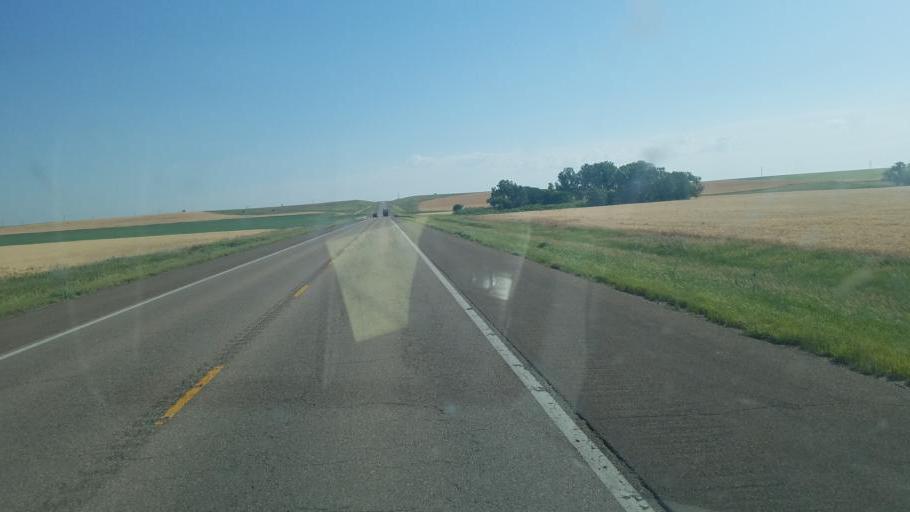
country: US
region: Kansas
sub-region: Barton County
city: Great Bend
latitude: 38.3772
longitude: -98.6867
